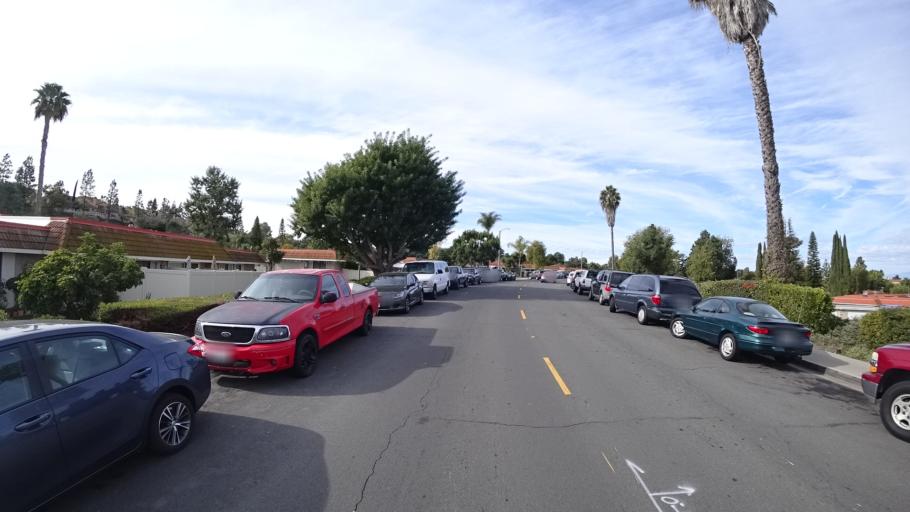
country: US
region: California
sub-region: Orange County
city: Laguna Woods
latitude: 33.6005
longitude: -117.7196
